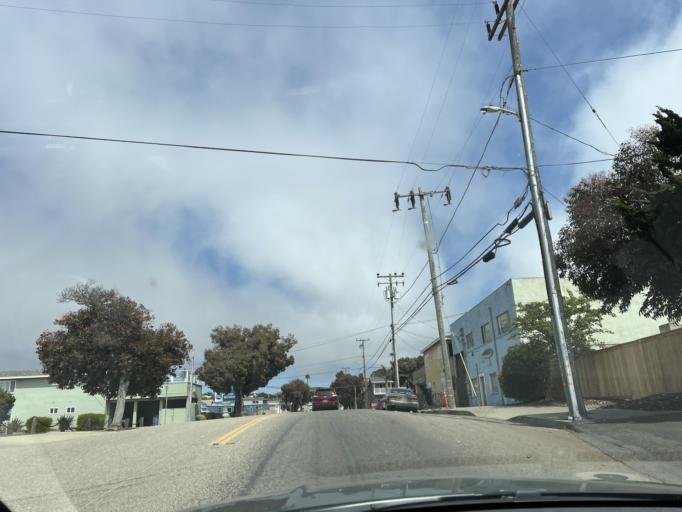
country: US
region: California
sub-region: San Luis Obispo County
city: Morro Bay
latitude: 35.3687
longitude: -120.8535
